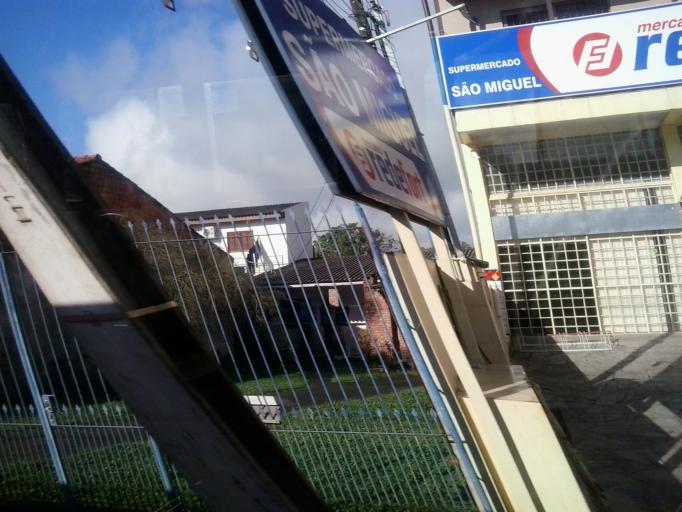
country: BR
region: Rio Grande do Sul
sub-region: Santa Maria
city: Santa Maria
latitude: -29.7082
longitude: -53.7263
